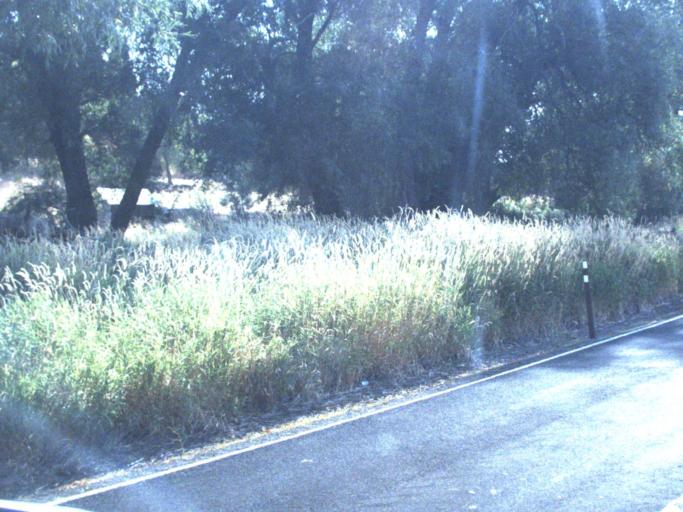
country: US
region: Washington
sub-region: Whitman County
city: Colfax
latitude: 47.1172
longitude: -117.1923
